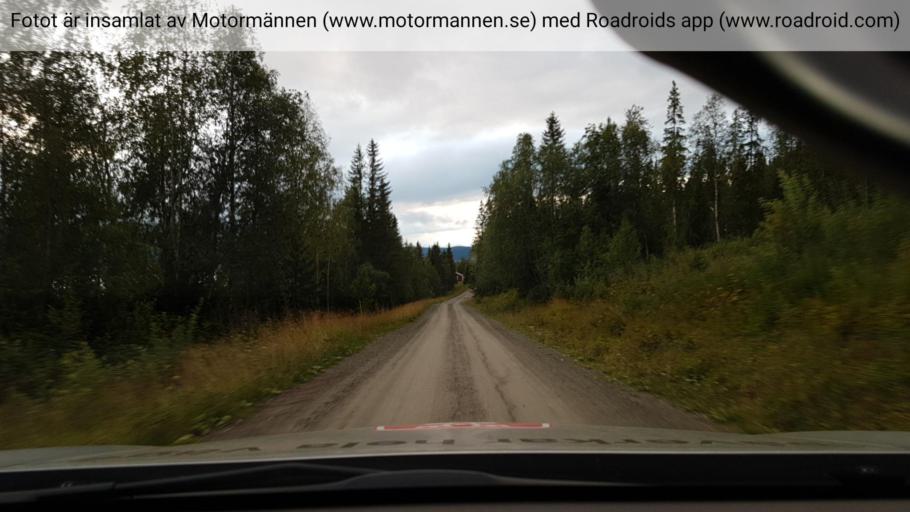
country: NO
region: Nordland
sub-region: Hattfjelldal
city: Hattfjelldal
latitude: 65.6155
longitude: 15.2535
